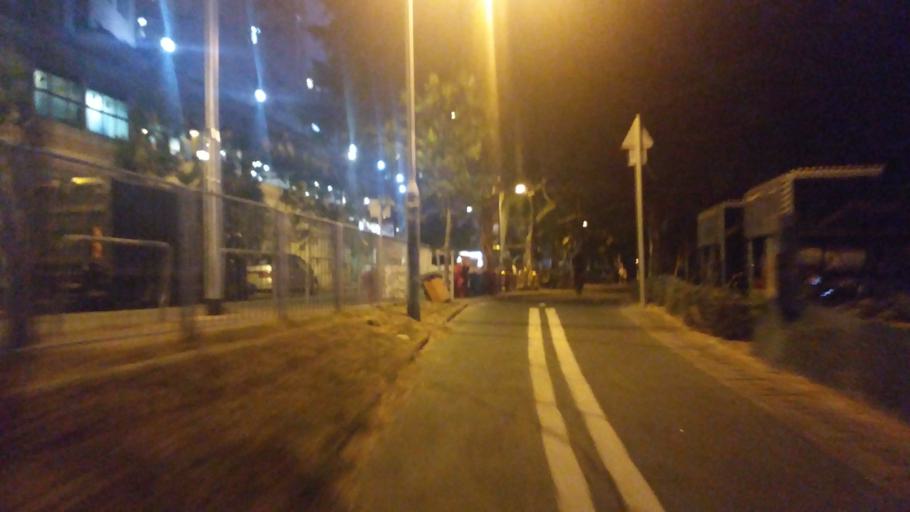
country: HK
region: Yuen Long
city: Yuen Long Kau Hui
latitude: 22.4346
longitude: 113.9959
